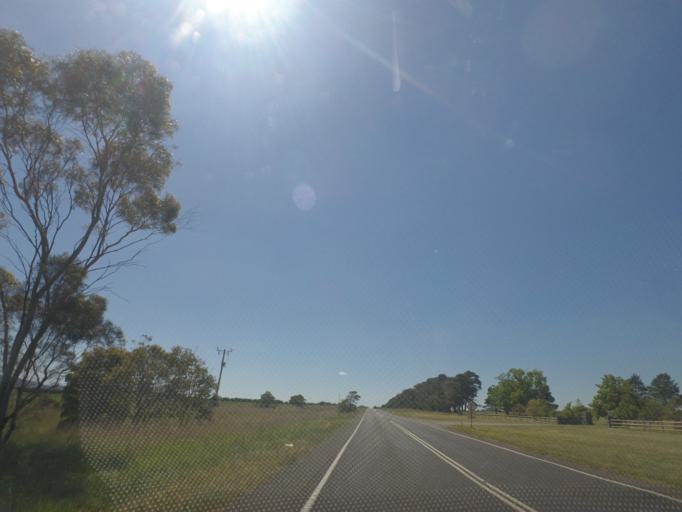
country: AU
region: Victoria
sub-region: Hume
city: Sunbury
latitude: -37.4610
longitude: 144.7415
